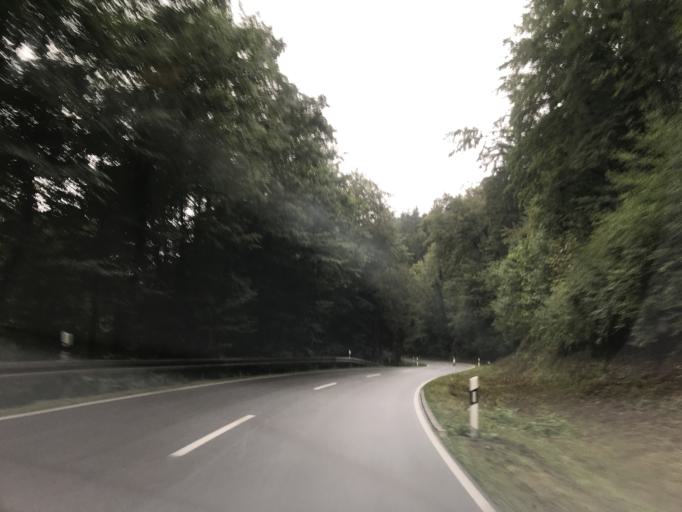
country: DE
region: Baden-Wuerttemberg
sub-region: Freiburg Region
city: Schworstadt
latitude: 47.5955
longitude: 7.8666
